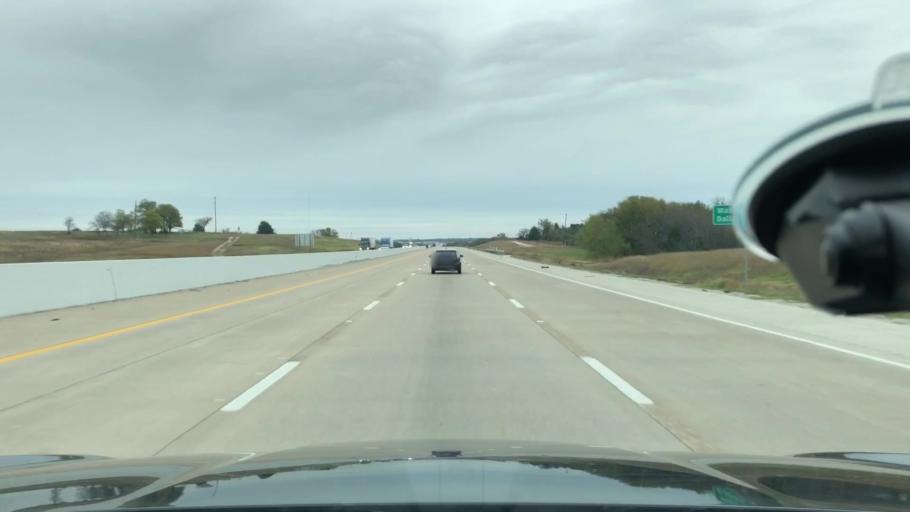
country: US
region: Texas
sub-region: Ellis County
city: Italy
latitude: 32.2104
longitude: -96.8922
